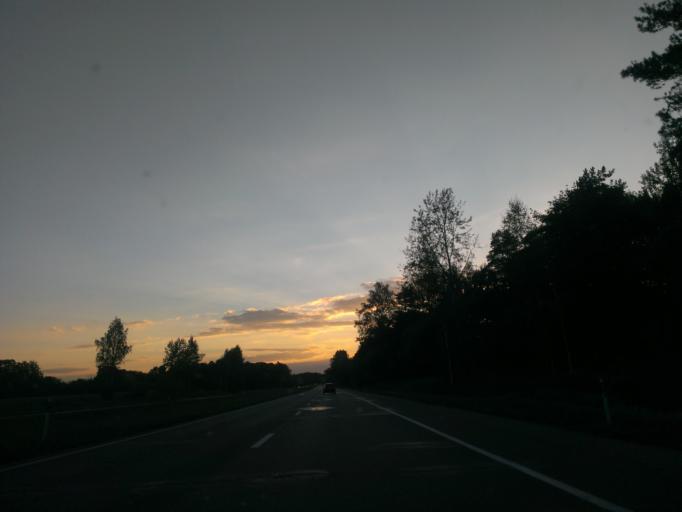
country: LV
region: Incukalns
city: Incukalns
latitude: 57.1264
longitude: 24.6955
